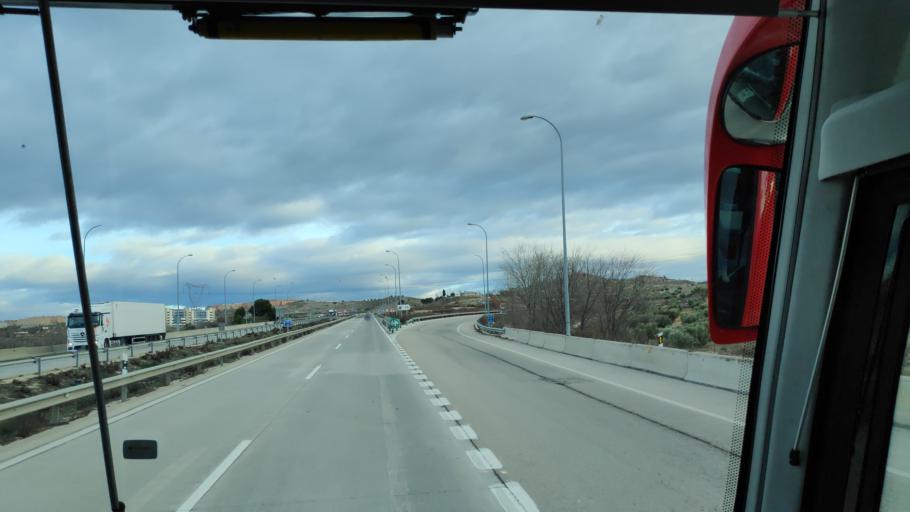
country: ES
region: Madrid
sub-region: Provincia de Madrid
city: Arganda
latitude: 40.2968
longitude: -3.4724
